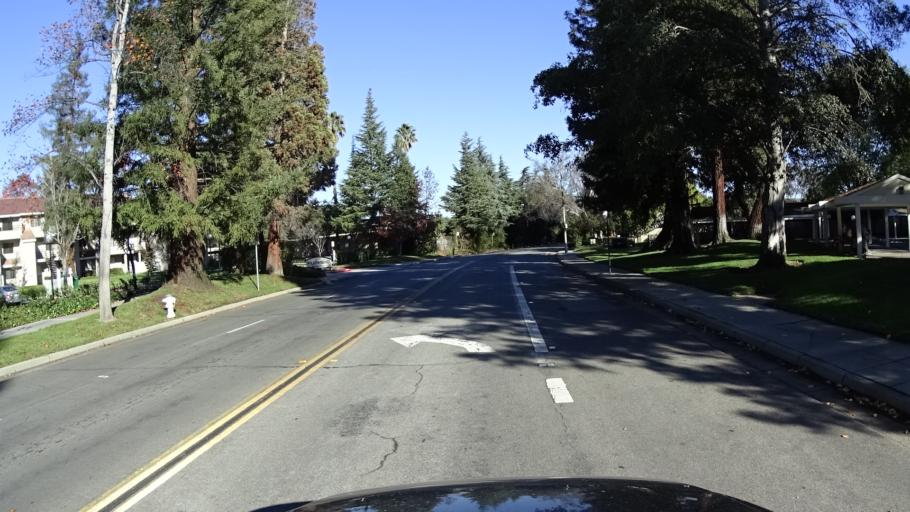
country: US
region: California
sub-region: Santa Clara County
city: Sunnyvale
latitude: 37.3689
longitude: -122.0033
